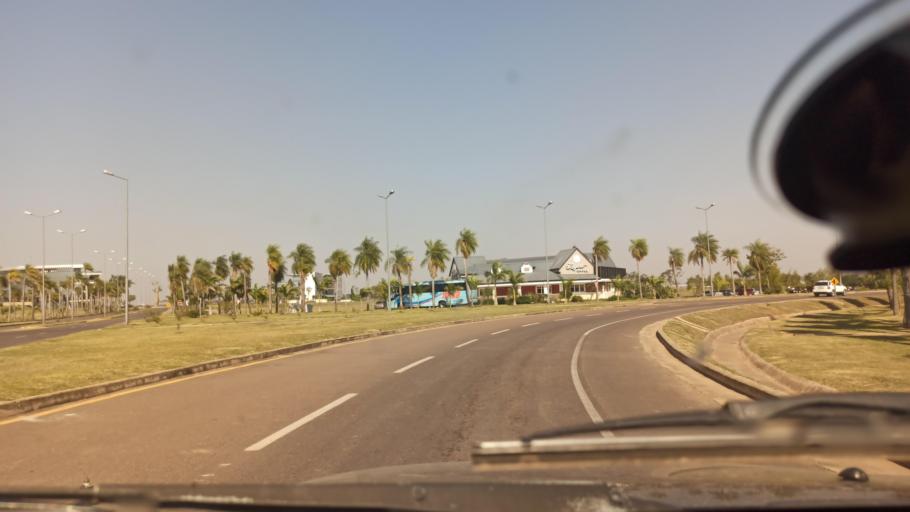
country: PY
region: Central
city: Colonia Mariano Roque Alonso
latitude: -25.1961
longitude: -57.5690
